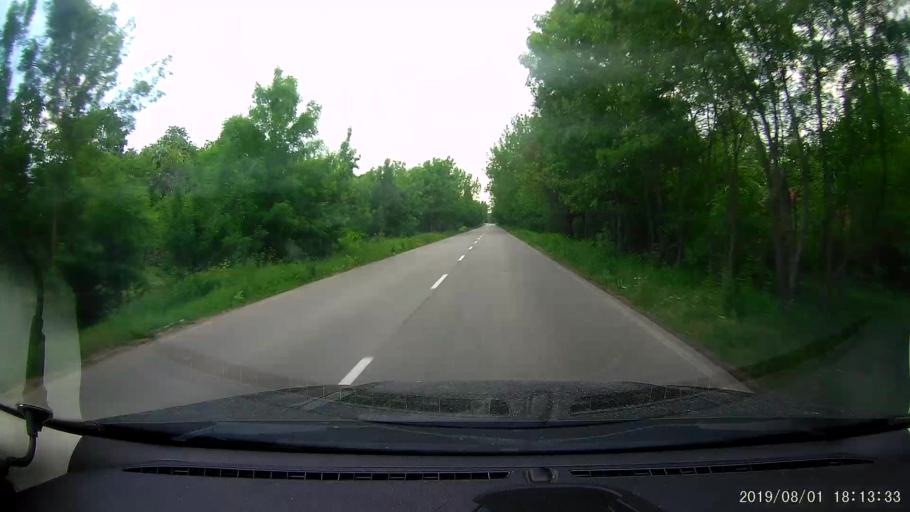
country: BG
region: Silistra
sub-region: Obshtina Dulovo
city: Dulovo
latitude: 43.7871
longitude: 27.1374
